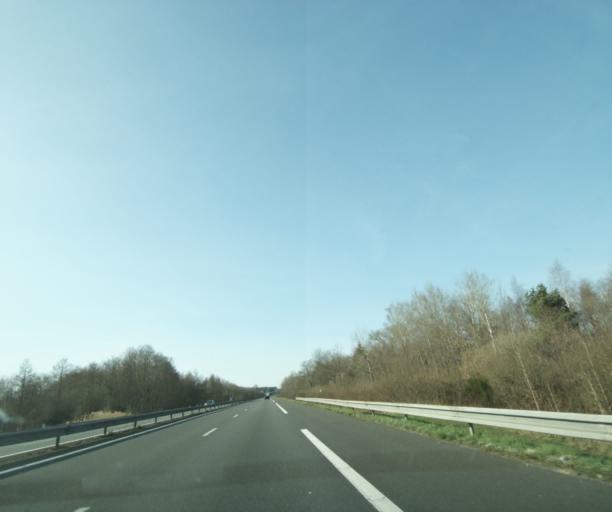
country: FR
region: Centre
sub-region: Departement du Loiret
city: La Ferte-Saint-Aubin
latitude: 47.7225
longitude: 1.8889
